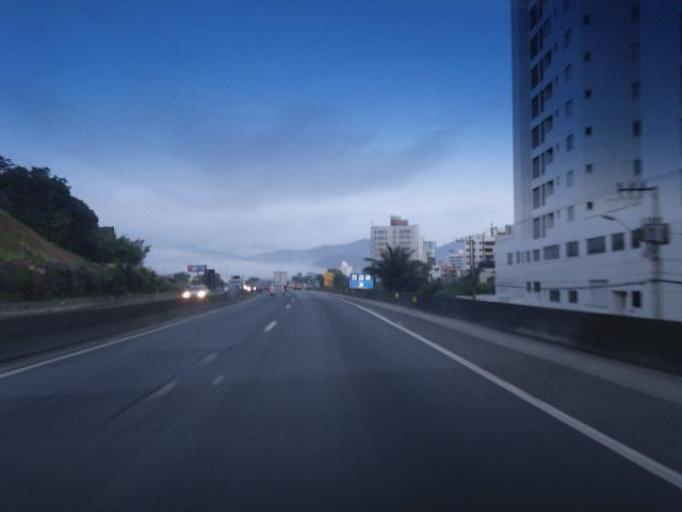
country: BR
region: Santa Catarina
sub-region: Itapema
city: Itapema
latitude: -27.1097
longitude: -48.6121
